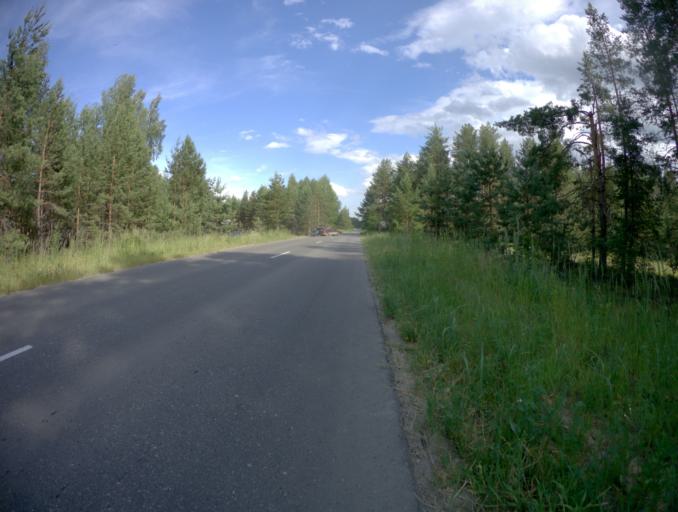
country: RU
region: Nizjnij Novgorod
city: Frolishchi
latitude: 56.3469
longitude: 42.7480
